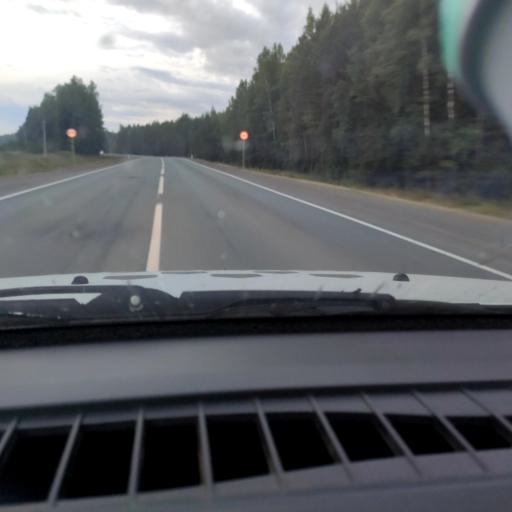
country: RU
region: Kirov
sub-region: Kirovo-Chepetskiy Rayon
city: Kirov
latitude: 58.6950
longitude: 49.6183
